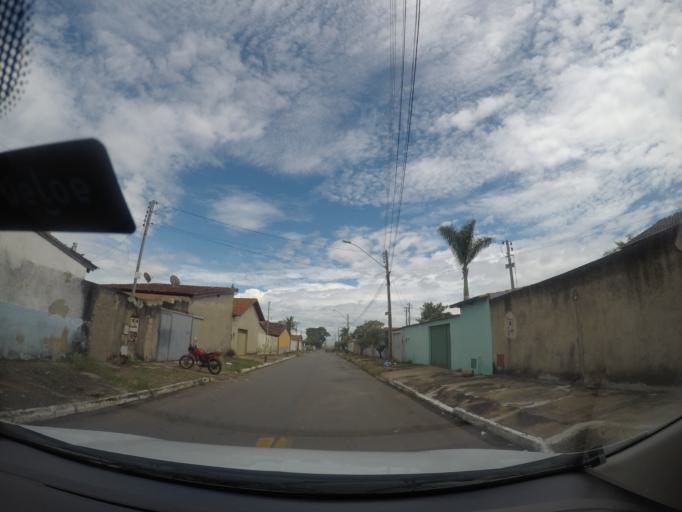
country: BR
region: Goias
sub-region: Aparecida De Goiania
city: Aparecida de Goiania
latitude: -16.7602
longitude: -49.3508
